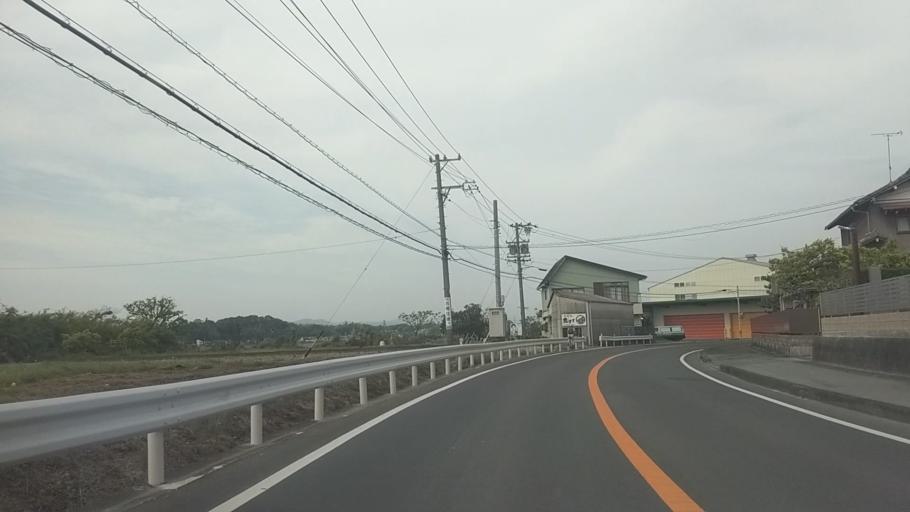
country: JP
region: Shizuoka
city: Kosai-shi
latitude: 34.7299
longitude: 137.6335
